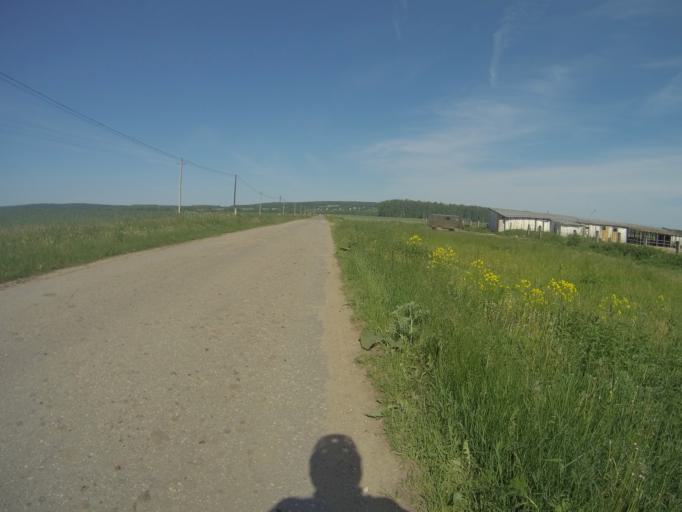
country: RU
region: Vladimir
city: Vorsha
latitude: 56.1094
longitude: 40.0755
